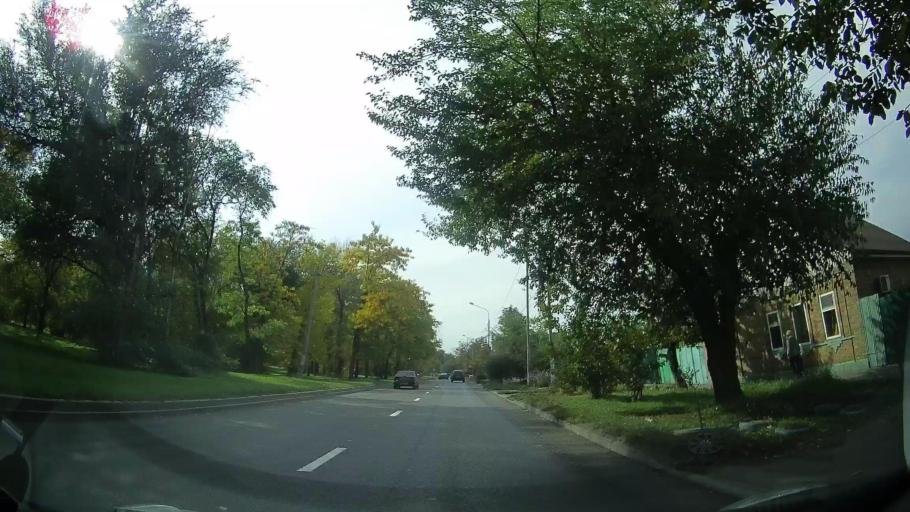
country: RU
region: Rostov
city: Severnyy
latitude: 47.2602
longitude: 39.7025
